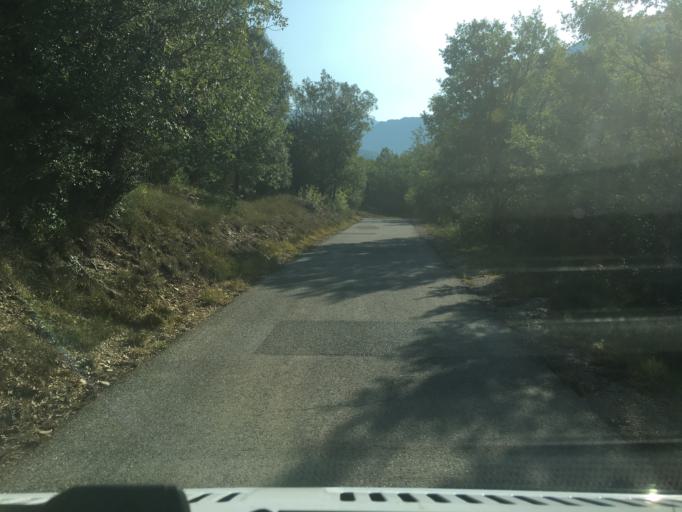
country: FR
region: Provence-Alpes-Cote d'Azur
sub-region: Departement des Alpes-de-Haute-Provence
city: Mallemoisson
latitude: 43.9452
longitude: 6.2060
